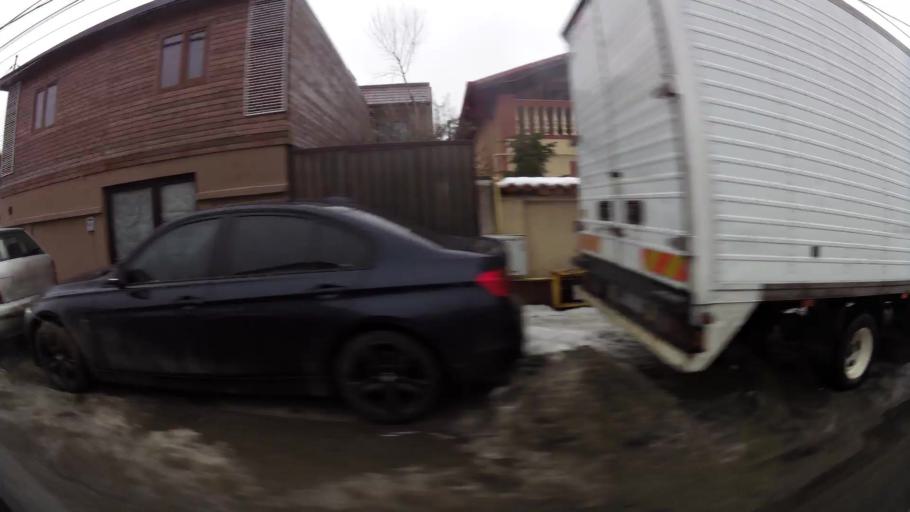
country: RO
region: Ilfov
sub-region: Comuna Chiajna
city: Chiajna
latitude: 44.4564
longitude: 25.9763
